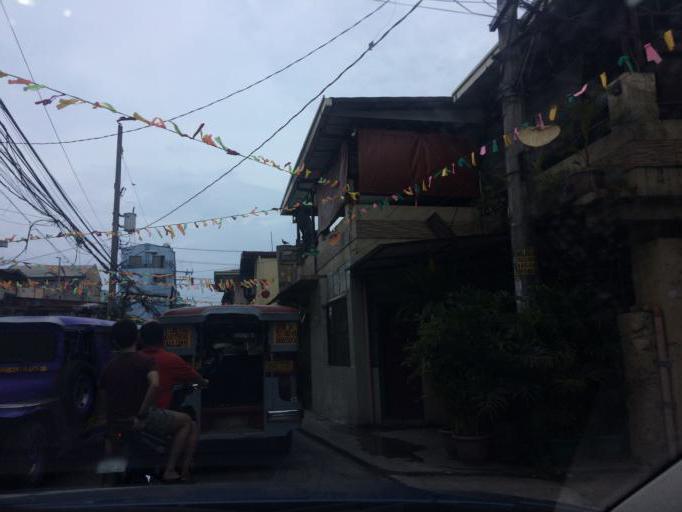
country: PH
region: Metro Manila
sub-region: Makati City
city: Makati City
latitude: 14.5474
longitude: 121.0022
